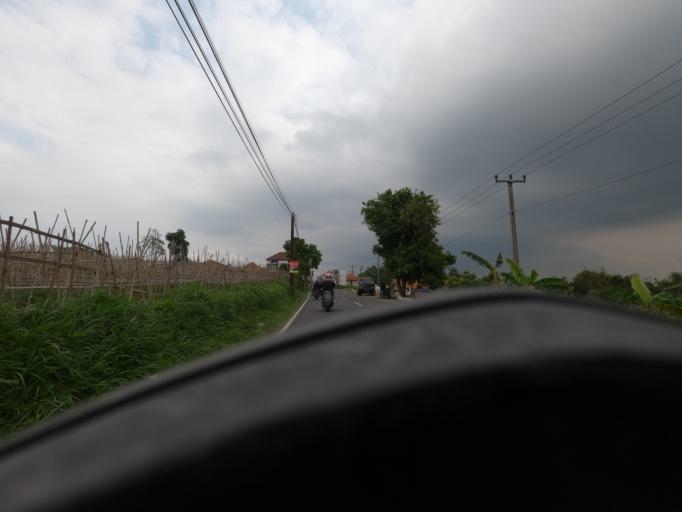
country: ID
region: West Java
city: Cimahi
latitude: -6.8222
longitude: 107.5342
